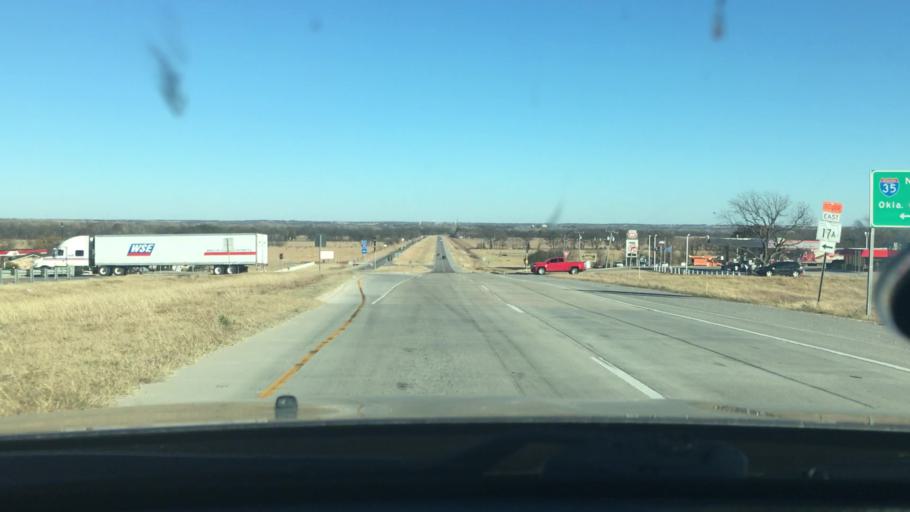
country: US
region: Oklahoma
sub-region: Murray County
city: Davis
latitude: 34.5064
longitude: -97.1734
